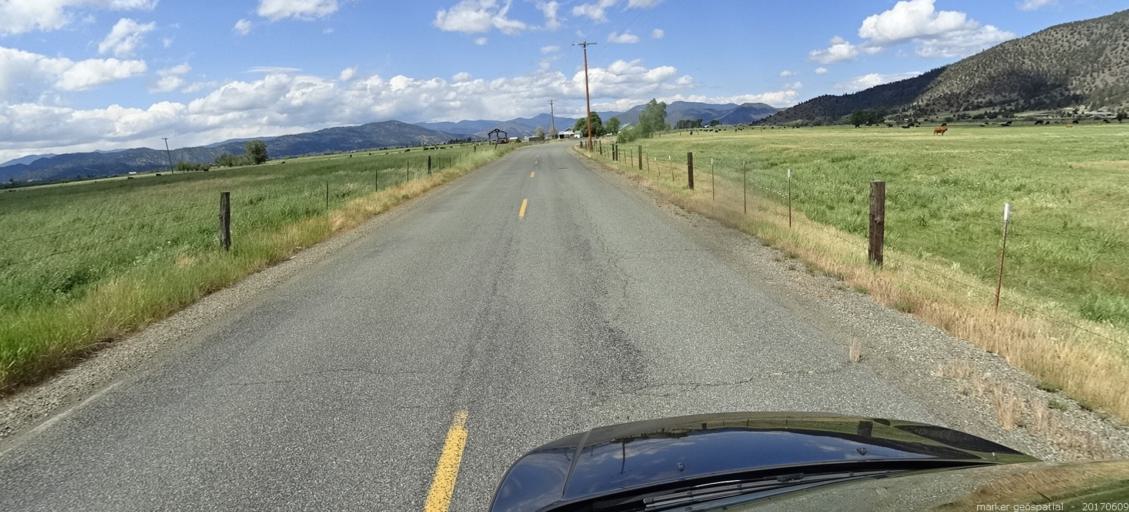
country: US
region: California
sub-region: Siskiyou County
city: Yreka
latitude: 41.5073
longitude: -122.8566
